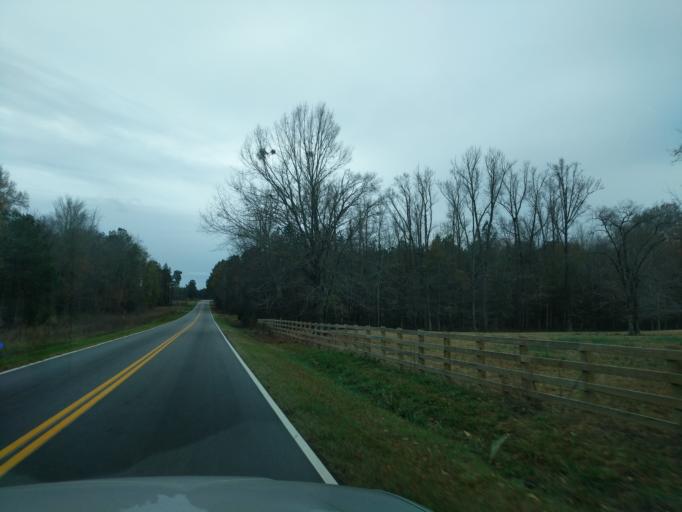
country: US
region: South Carolina
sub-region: Laurens County
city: Laurens
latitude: 34.3434
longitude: -81.9923
